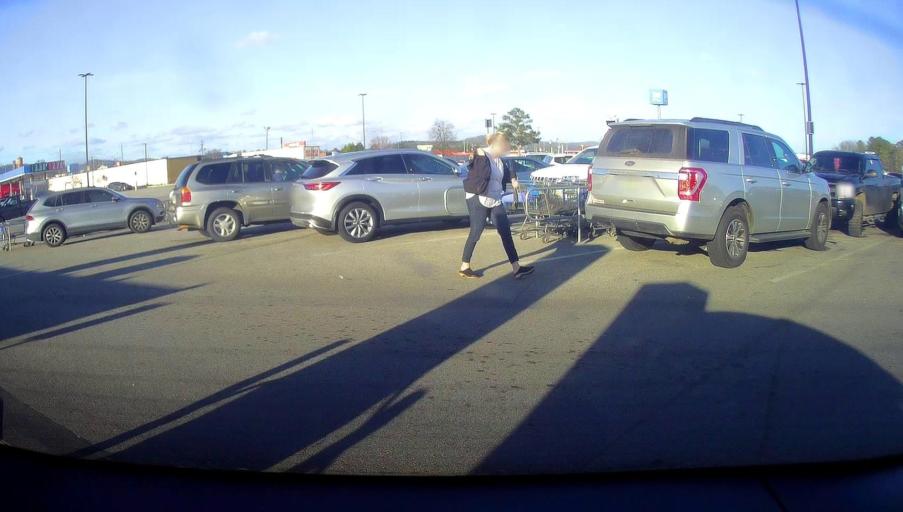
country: US
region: Alabama
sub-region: Calhoun County
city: Oxford
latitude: 33.5996
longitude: -85.8339
